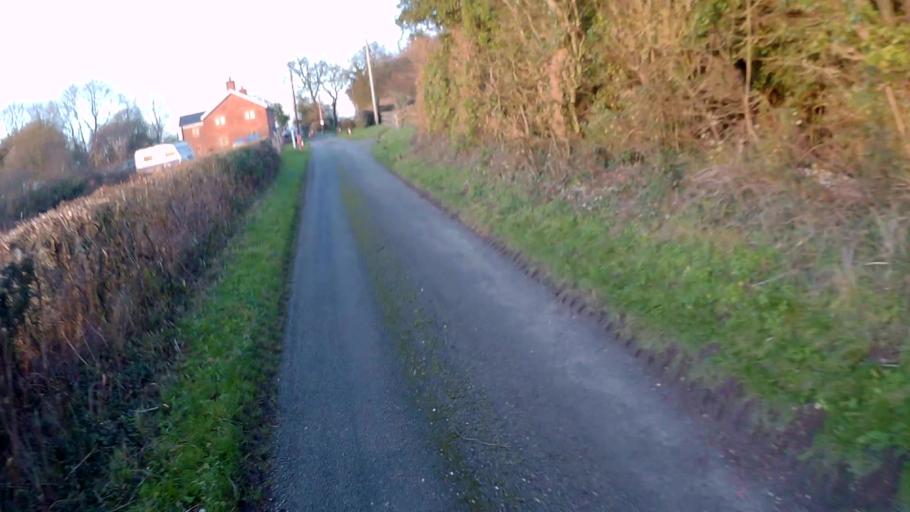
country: GB
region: England
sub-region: Hampshire
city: Overton
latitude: 51.2127
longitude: -1.2456
